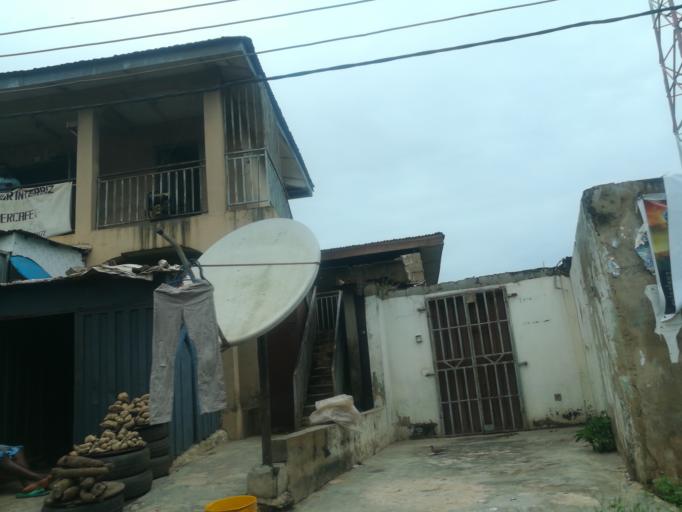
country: NG
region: Oyo
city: Ibadan
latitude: 7.3393
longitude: 3.9068
